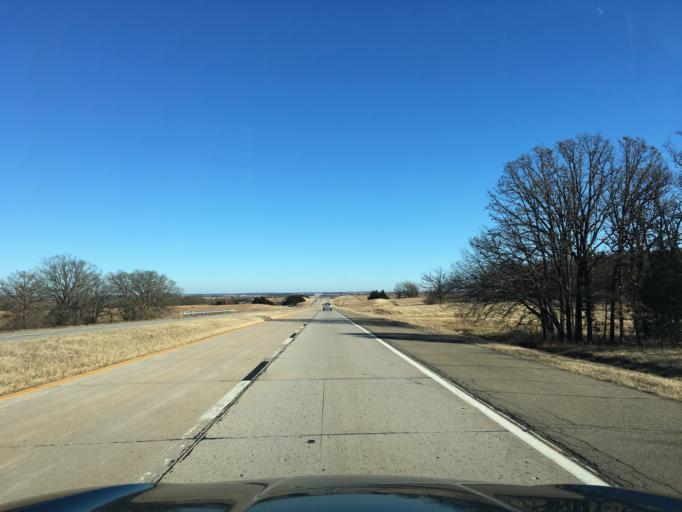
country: US
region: Oklahoma
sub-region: Payne County
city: Yale
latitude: 36.2240
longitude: -96.7449
